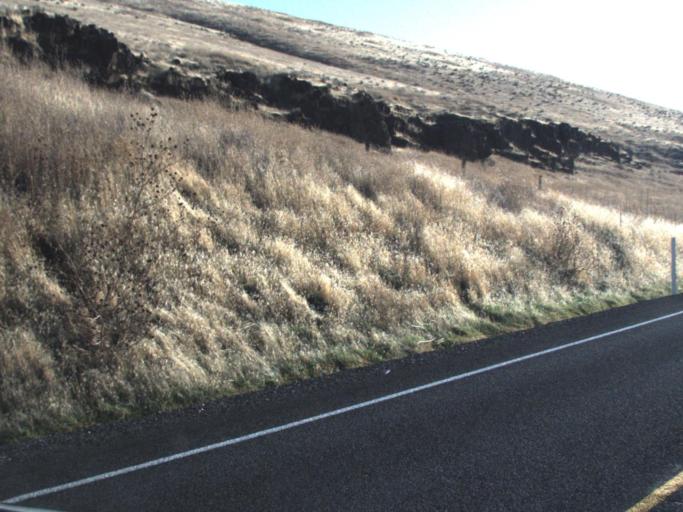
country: US
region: Washington
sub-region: Garfield County
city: Pomeroy
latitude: 46.4949
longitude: -117.7707
